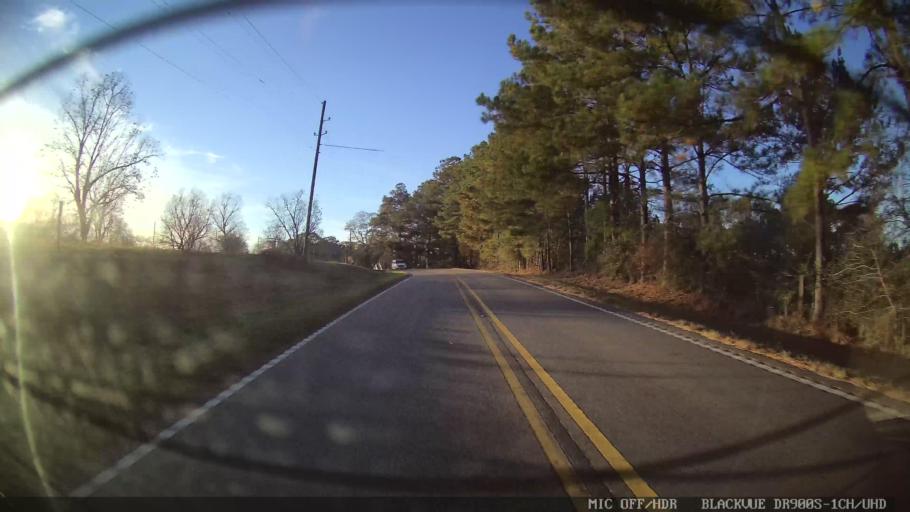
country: US
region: Mississippi
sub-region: Lamar County
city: Lumberton
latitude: 30.9952
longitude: -89.3844
